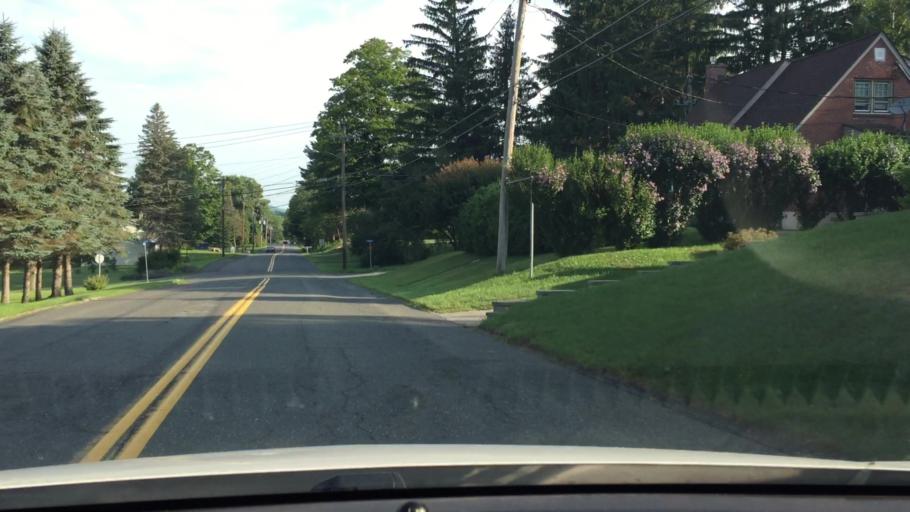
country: US
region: Massachusetts
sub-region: Berkshire County
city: Lee
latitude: 42.3129
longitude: -73.2335
